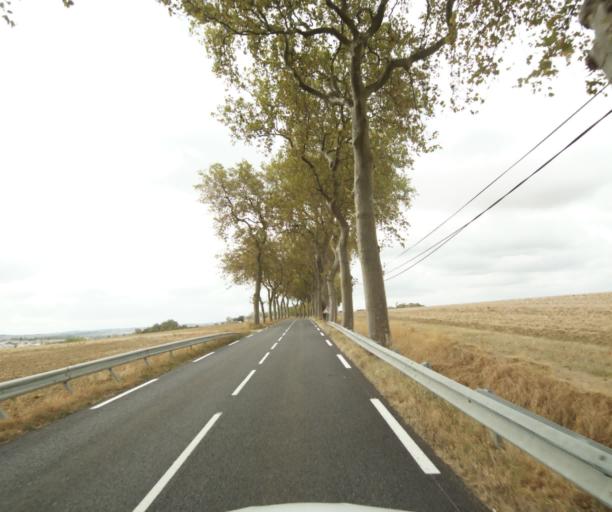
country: FR
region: Midi-Pyrenees
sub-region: Departement de la Haute-Garonne
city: Villefranche-de-Lauragais
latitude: 43.4168
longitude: 1.7175
